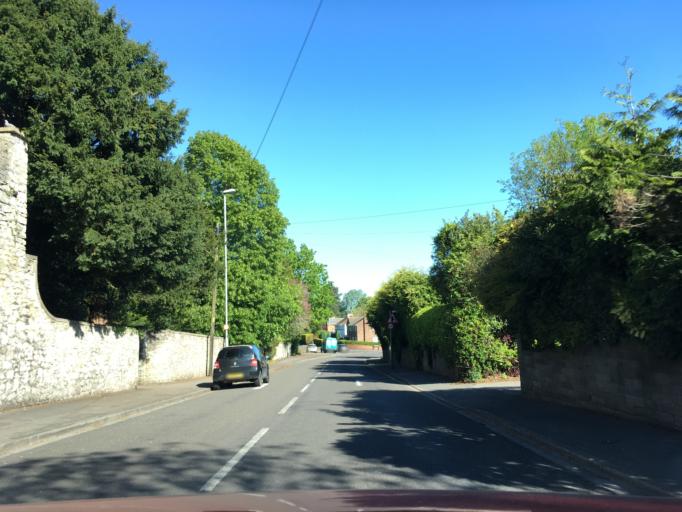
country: GB
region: England
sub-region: South Gloucestershire
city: Severn Beach
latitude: 51.5071
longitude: -2.6345
